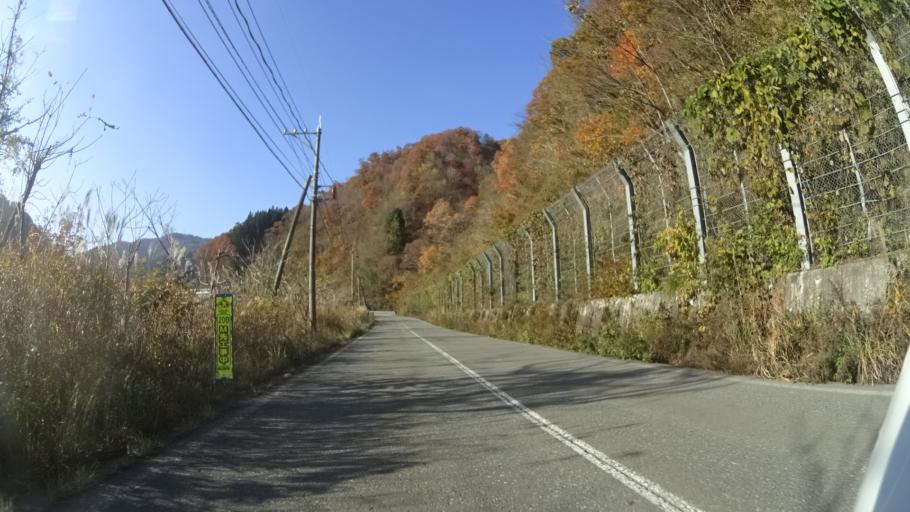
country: JP
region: Fukui
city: Ono
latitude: 35.9020
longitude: 136.6781
